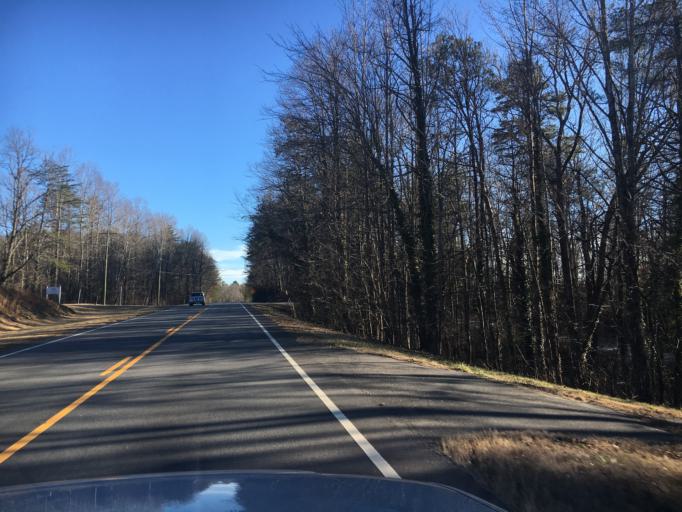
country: US
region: Georgia
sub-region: White County
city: Cleveland
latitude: 34.6651
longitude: -83.8568
